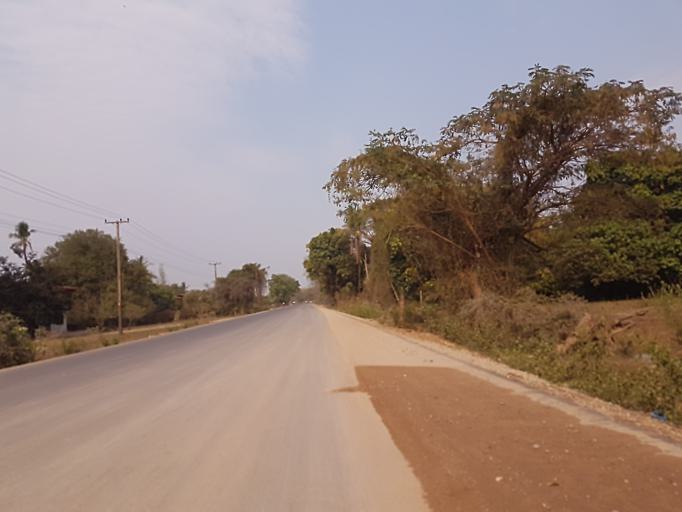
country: TH
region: Nong Khai
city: Nong Khai
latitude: 17.9607
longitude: 102.8338
